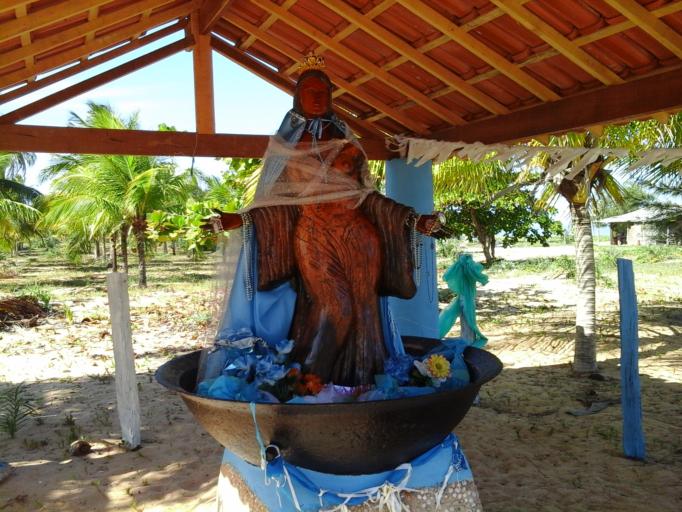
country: BR
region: Bahia
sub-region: Nova Vicosa
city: Nova Vicosa
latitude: -17.7019
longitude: -39.1483
